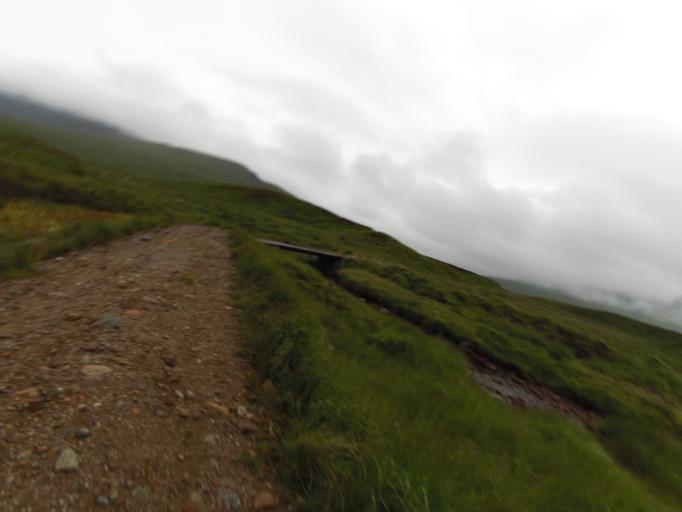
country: GB
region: Scotland
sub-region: Highland
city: Spean Bridge
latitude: 56.7638
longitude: -4.6982
